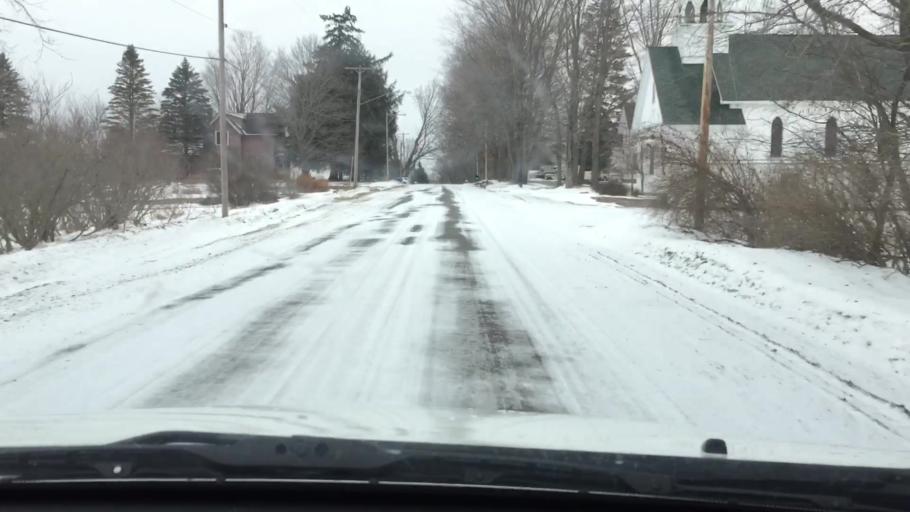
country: US
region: Michigan
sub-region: Osceola County
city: Reed City
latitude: 44.0352
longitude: -85.4524
